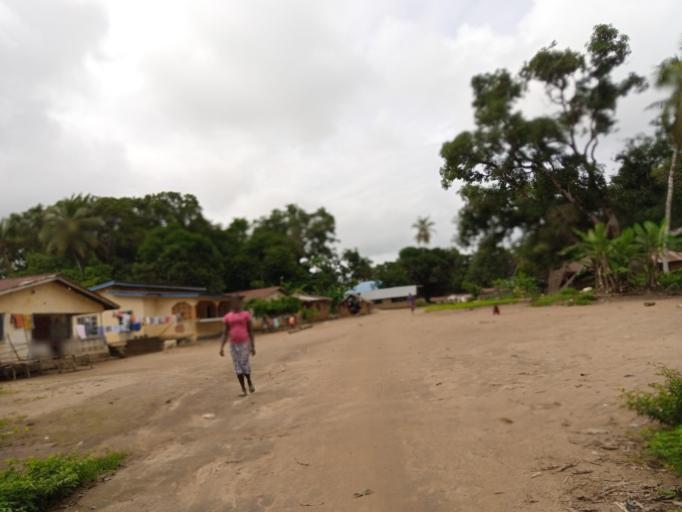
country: SL
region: Northern Province
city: Masoyila
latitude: 8.5785
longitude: -13.1890
